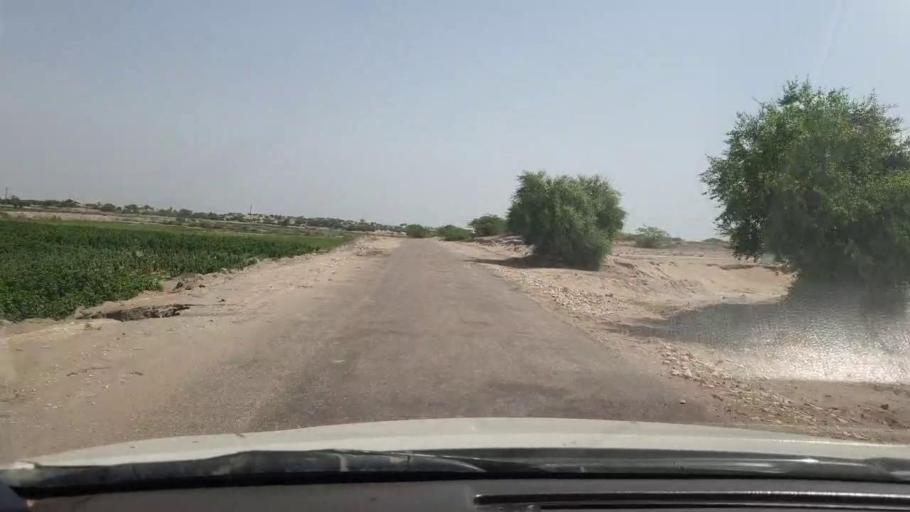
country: PK
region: Sindh
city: Rohri
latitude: 27.4849
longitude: 69.0549
